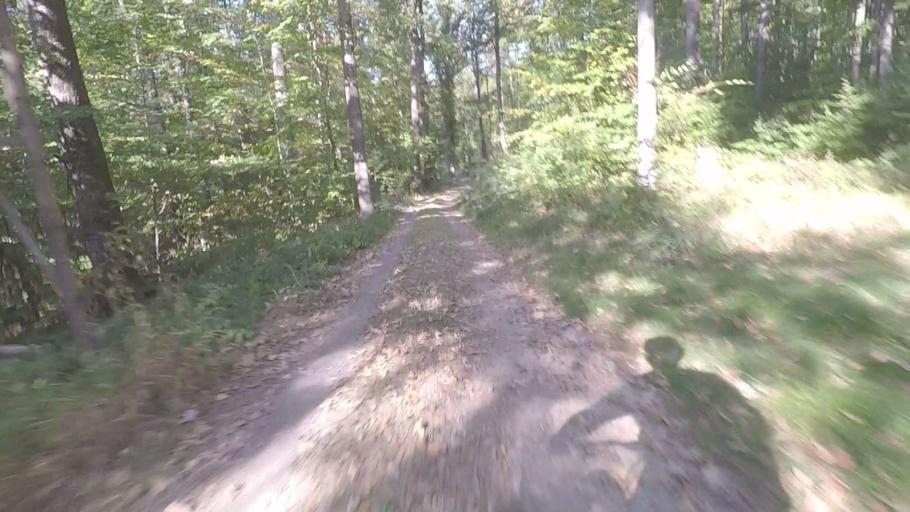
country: DE
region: Baden-Wuerttemberg
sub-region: Regierungsbezirk Stuttgart
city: Spiegelberg
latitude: 49.0400
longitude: 9.4791
